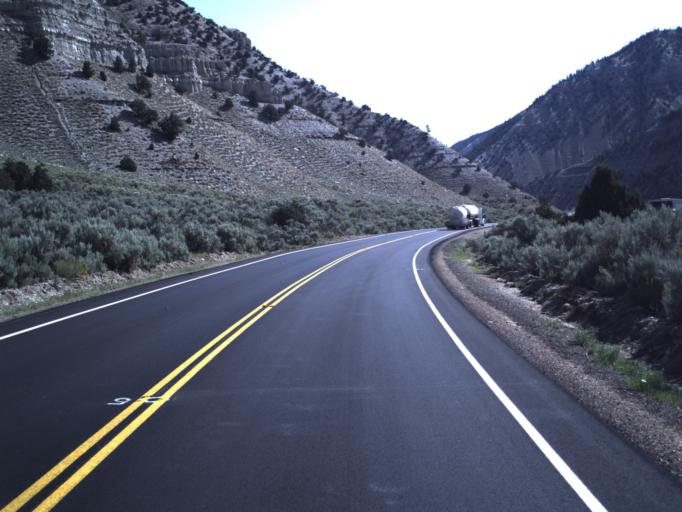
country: US
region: Utah
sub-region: Duchesne County
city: Duchesne
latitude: 39.9706
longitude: -110.6314
